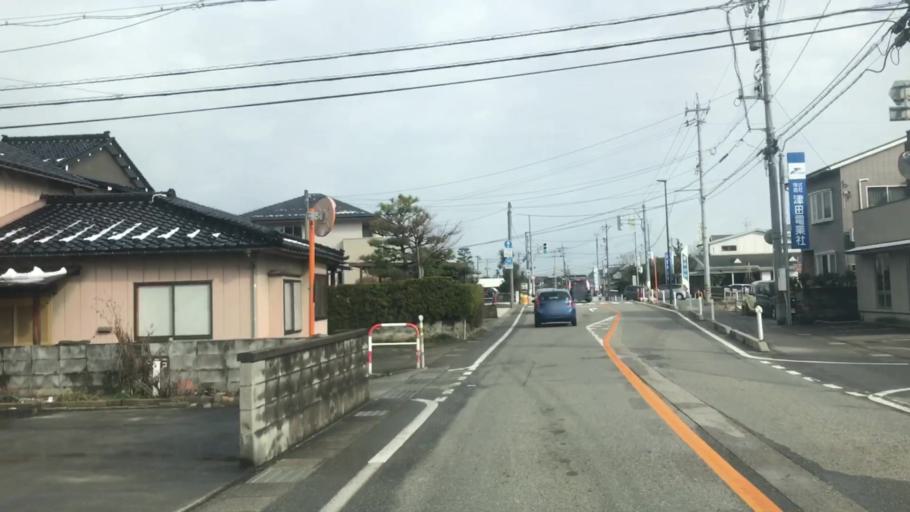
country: JP
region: Toyama
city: Toyama-shi
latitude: 36.6559
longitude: 137.2180
